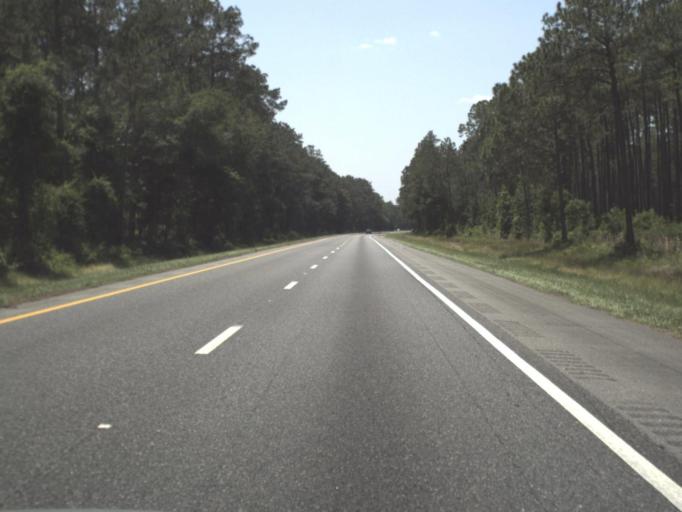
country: US
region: Florida
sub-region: Columbia County
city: Watertown
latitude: 30.2540
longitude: -82.5003
